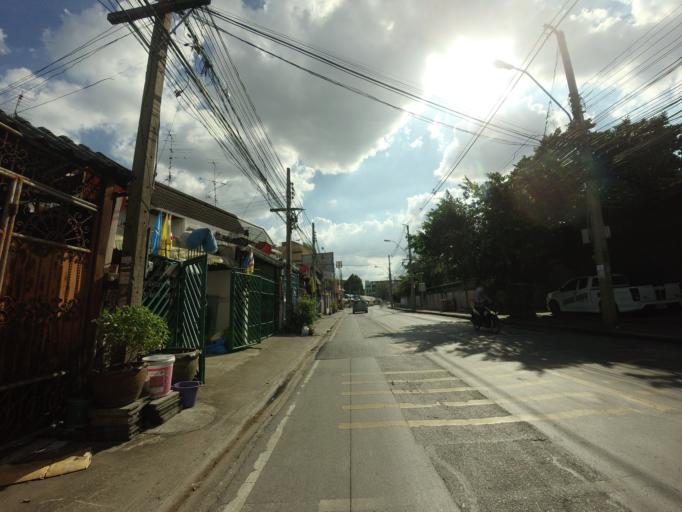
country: TH
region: Bangkok
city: Huai Khwang
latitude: 13.7810
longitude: 100.5866
